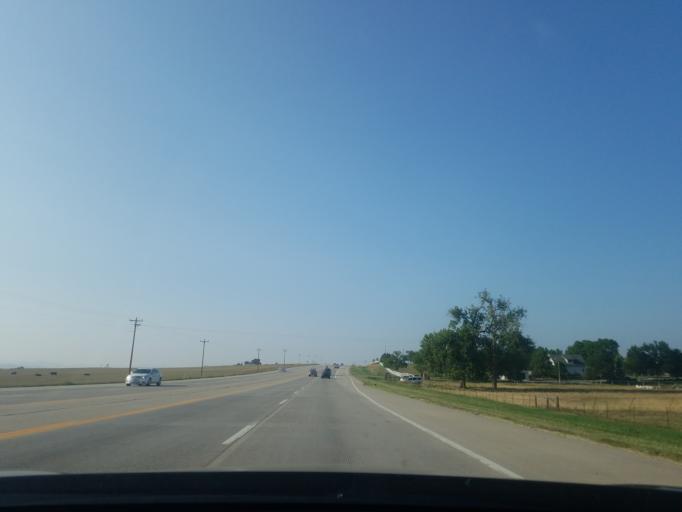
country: US
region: Colorado
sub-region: Boulder County
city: Longmont
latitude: 40.2391
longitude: -105.1026
